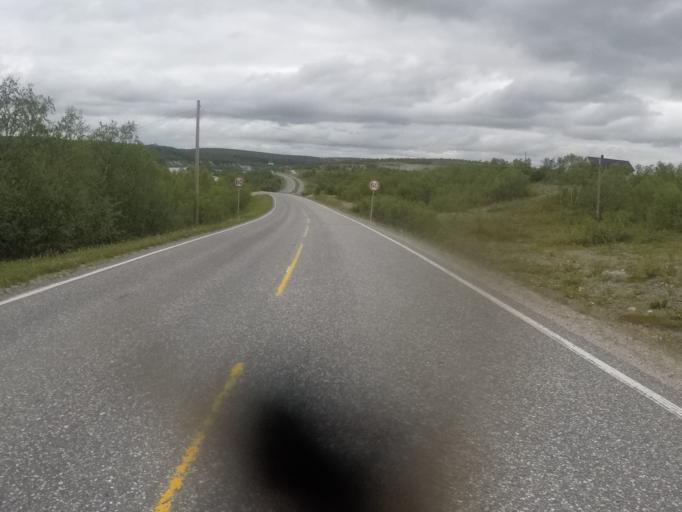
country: NO
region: Finnmark Fylke
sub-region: Kautokeino
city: Kautokeino
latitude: 68.9853
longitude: 23.0528
